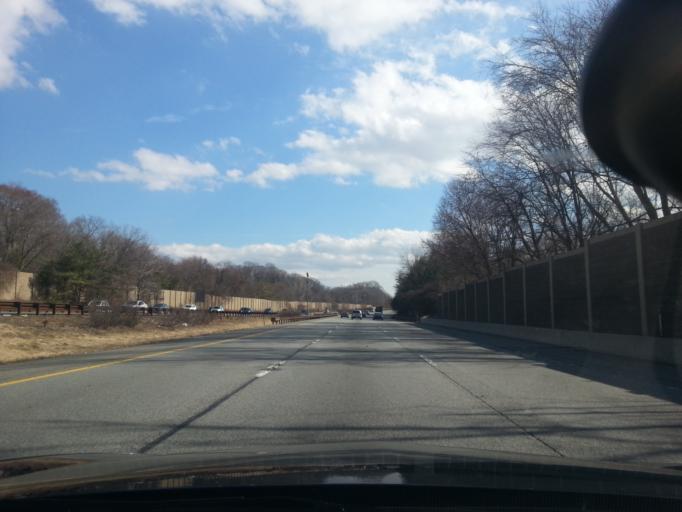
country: US
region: Pennsylvania
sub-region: Delaware County
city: Radnor
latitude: 40.0198
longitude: -75.3598
